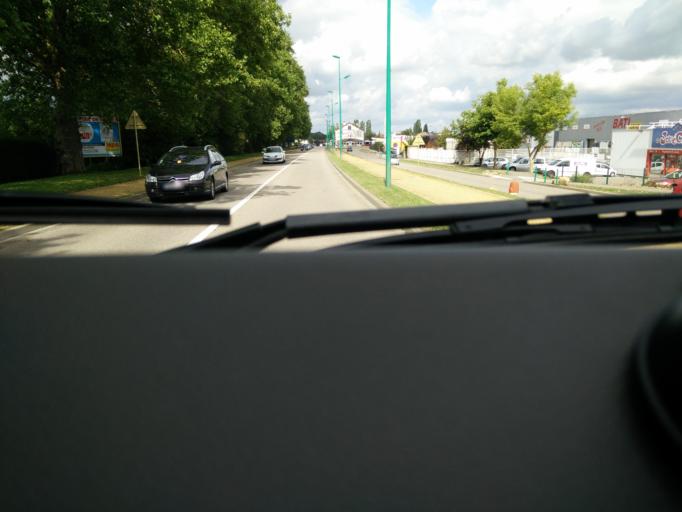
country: FR
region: Lorraine
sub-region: Departement de la Meuse
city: Verdun
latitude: 49.1466
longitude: 5.4052
